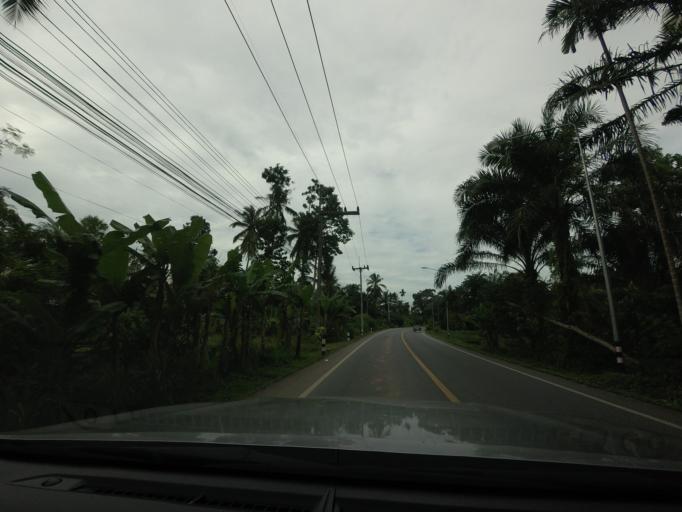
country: TH
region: Nakhon Si Thammarat
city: Phra Phrom
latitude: 8.3180
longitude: 99.9460
